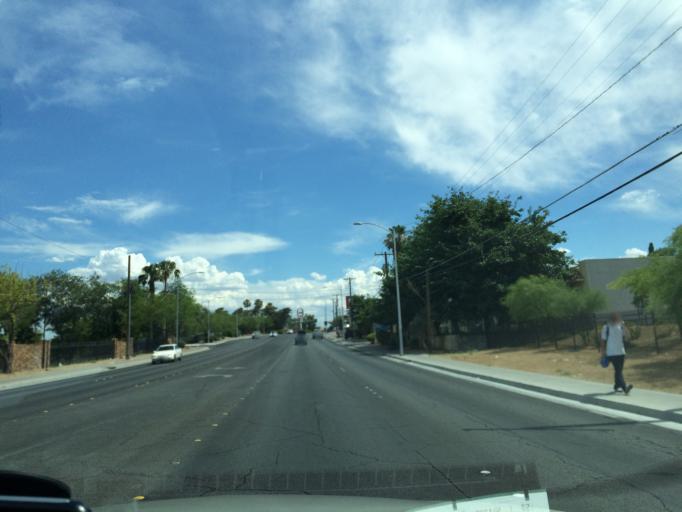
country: US
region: Nevada
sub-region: Clark County
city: Las Vegas
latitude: 36.1842
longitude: -115.1341
